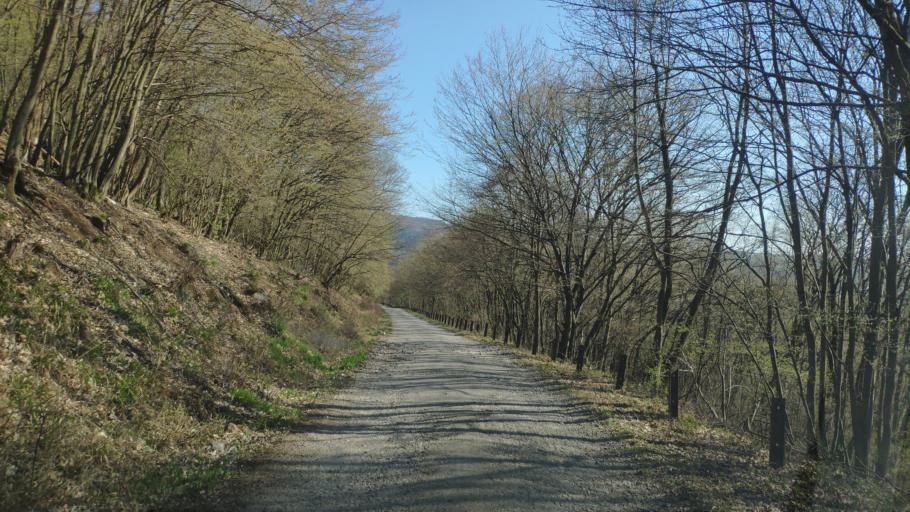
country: SK
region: Kosicky
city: Roznava
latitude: 48.5611
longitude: 20.4043
